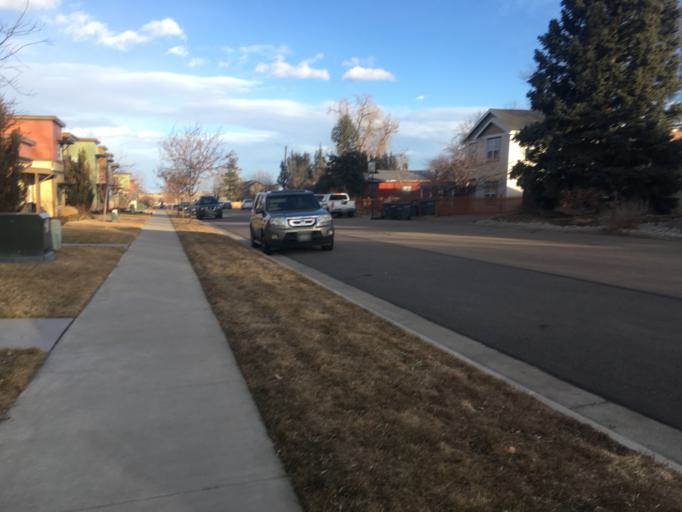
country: US
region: Colorado
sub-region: Boulder County
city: Lafayette
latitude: 40.0012
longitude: -105.0824
